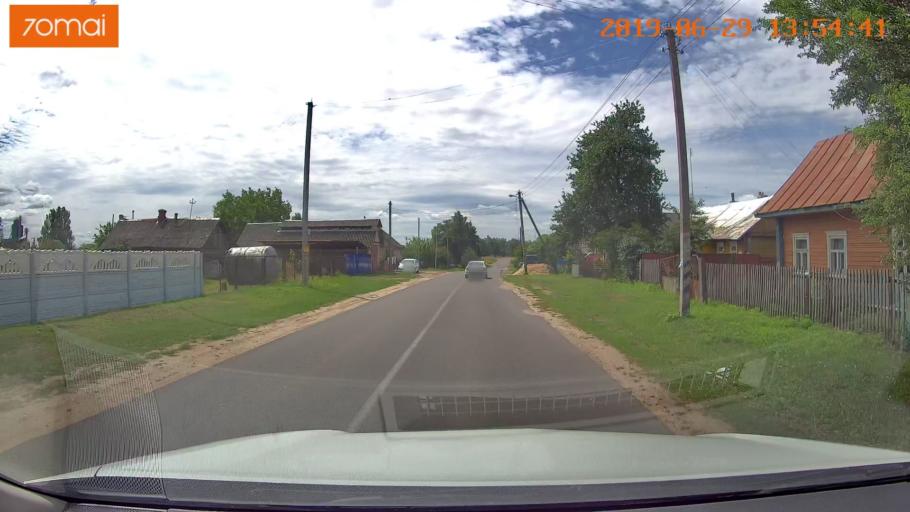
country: BY
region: Minsk
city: Slutsk
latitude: 52.9840
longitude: 27.5292
